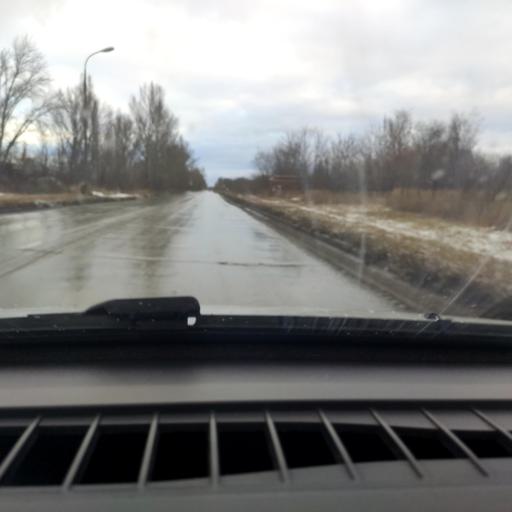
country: RU
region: Samara
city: Podstepki
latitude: 53.5734
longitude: 49.2186
